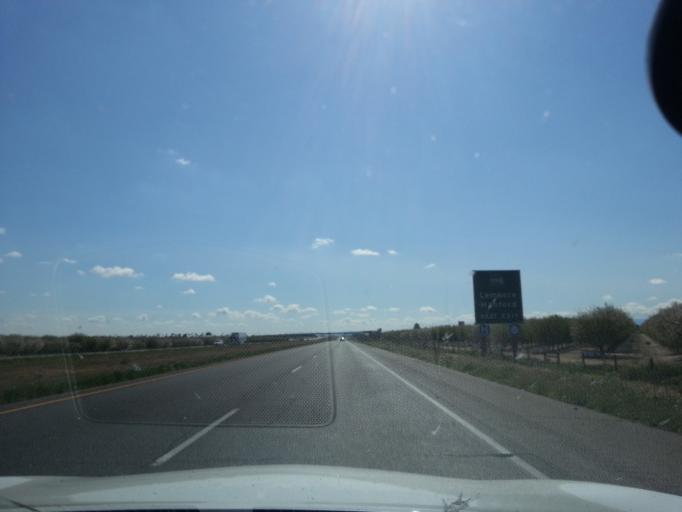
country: US
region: California
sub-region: Fresno County
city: Huron
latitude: 36.2642
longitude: -120.2504
